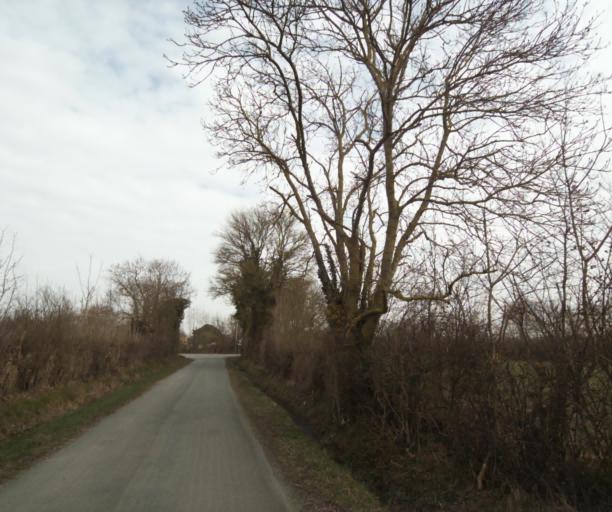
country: FR
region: Poitou-Charentes
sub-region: Departement des Deux-Sevres
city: Niort
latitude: 46.2933
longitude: -0.4726
